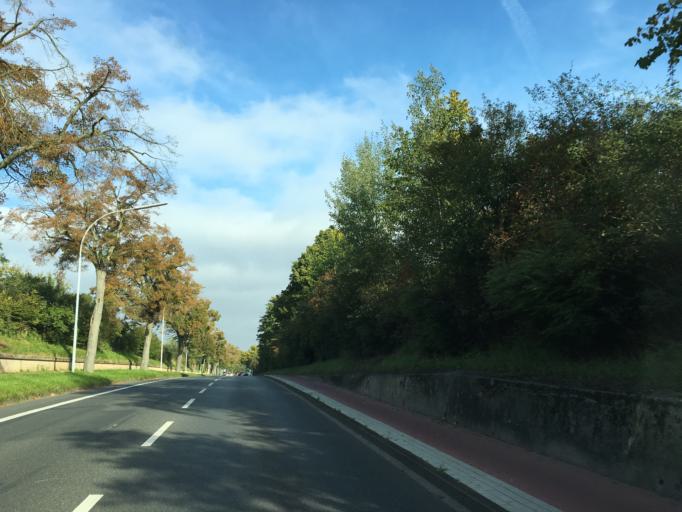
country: DE
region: Lower Saxony
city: Lueneburg
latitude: 53.2630
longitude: 10.4076
